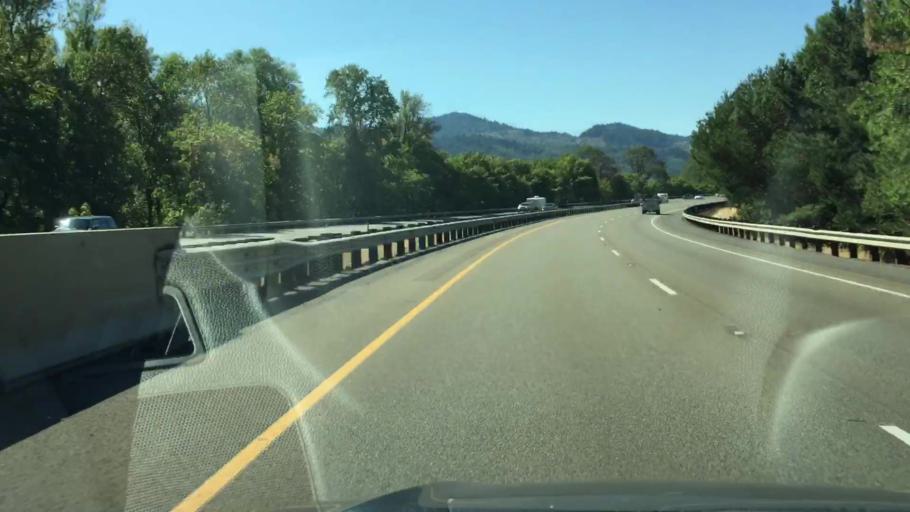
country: US
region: Oregon
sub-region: Douglas County
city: Myrtle Creek
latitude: 43.0149
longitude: -123.3015
